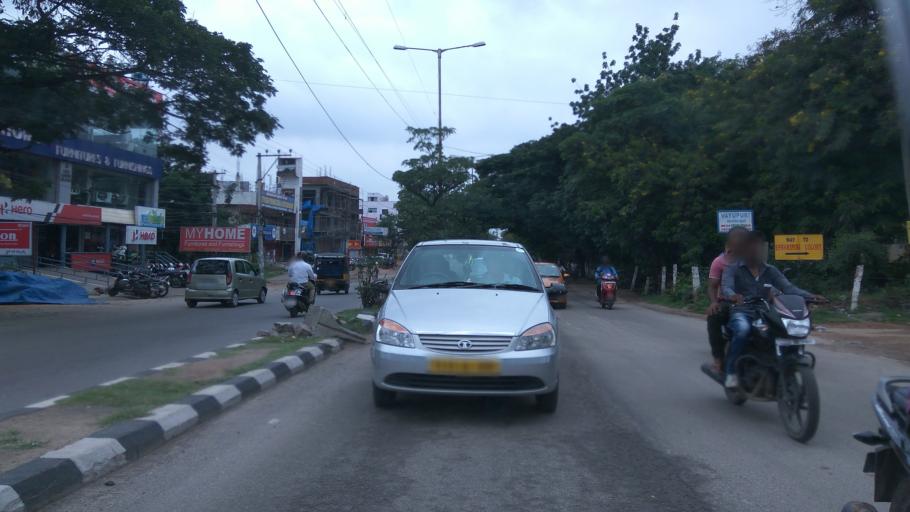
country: IN
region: Telangana
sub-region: Rangareddi
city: Secunderabad
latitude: 17.4837
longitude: 78.5465
